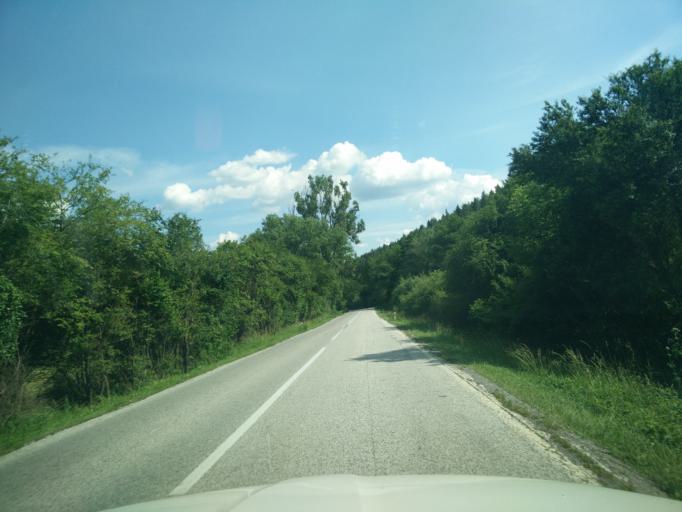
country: SK
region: Nitriansky
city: Prievidza
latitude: 48.9192
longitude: 18.6478
